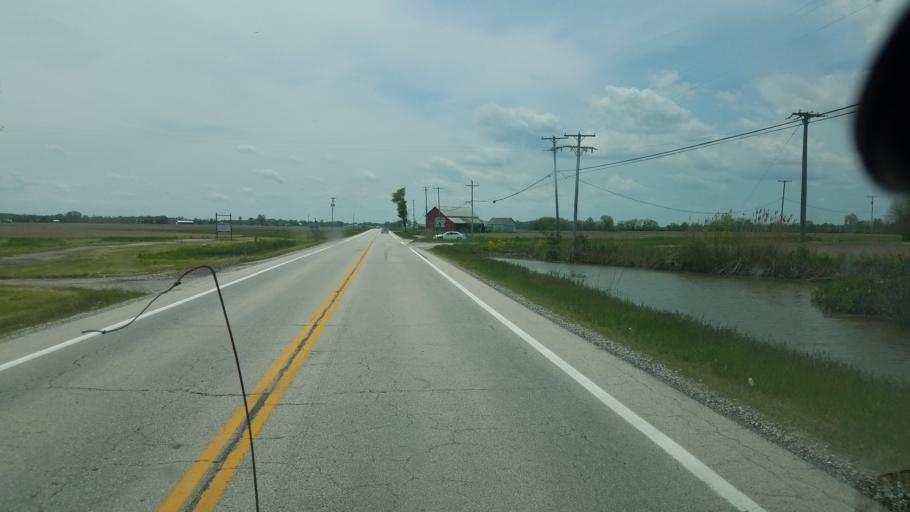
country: US
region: Ohio
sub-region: Ottawa County
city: Oak Harbor
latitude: 41.4433
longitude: -83.0621
